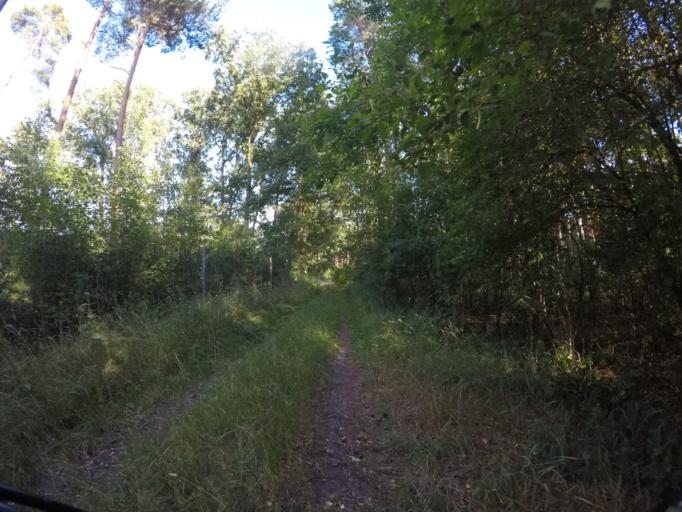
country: DE
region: Lower Saxony
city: Hitzacker
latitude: 53.2267
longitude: 11.0497
